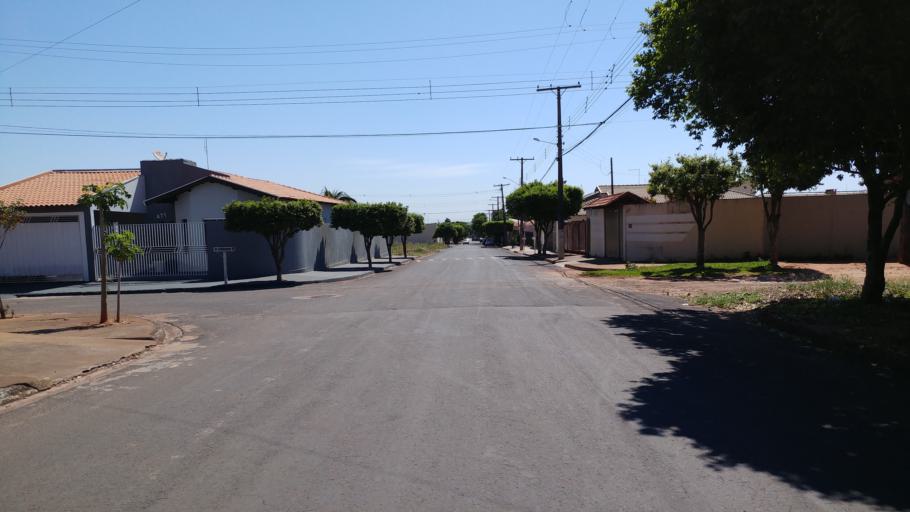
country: BR
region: Sao Paulo
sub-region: Paraguacu Paulista
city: Paraguacu Paulista
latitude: -22.4131
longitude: -50.5890
